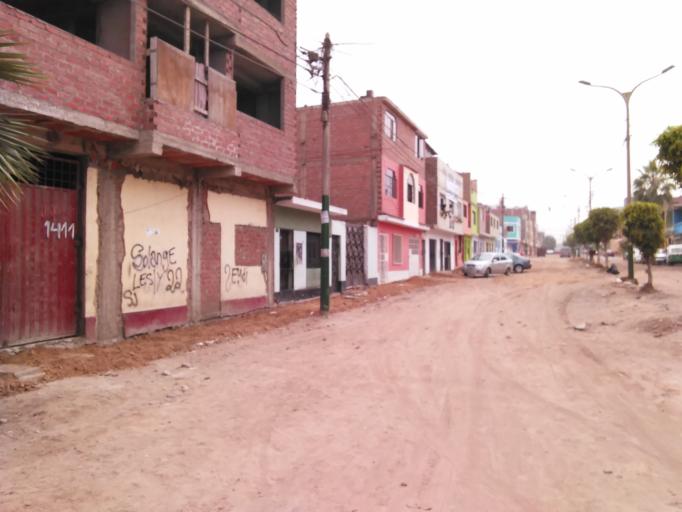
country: PE
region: Callao
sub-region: Callao
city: Callao
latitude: -12.0379
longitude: -77.0848
